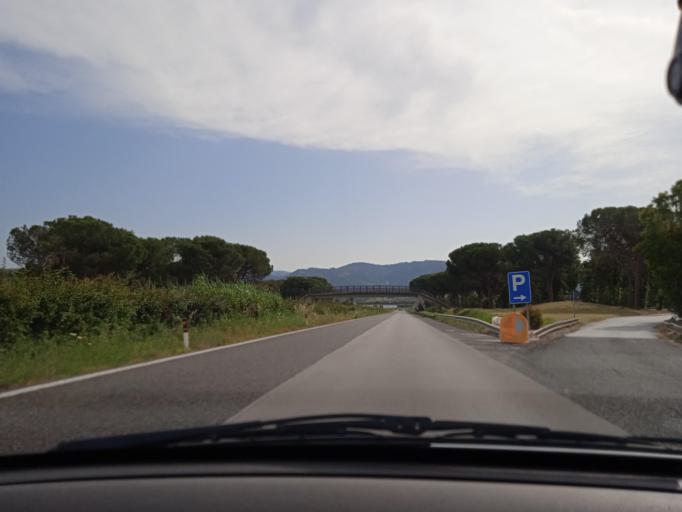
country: IT
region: Sicily
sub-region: Messina
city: Tonnarella
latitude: 38.1208
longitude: 15.1164
